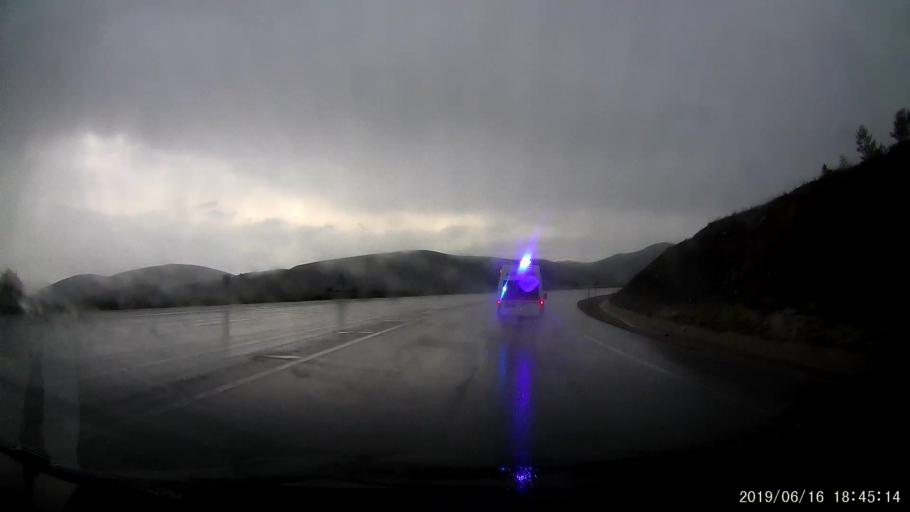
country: TR
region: Erzincan
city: Doganbeyli
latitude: 39.8712
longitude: 39.0606
